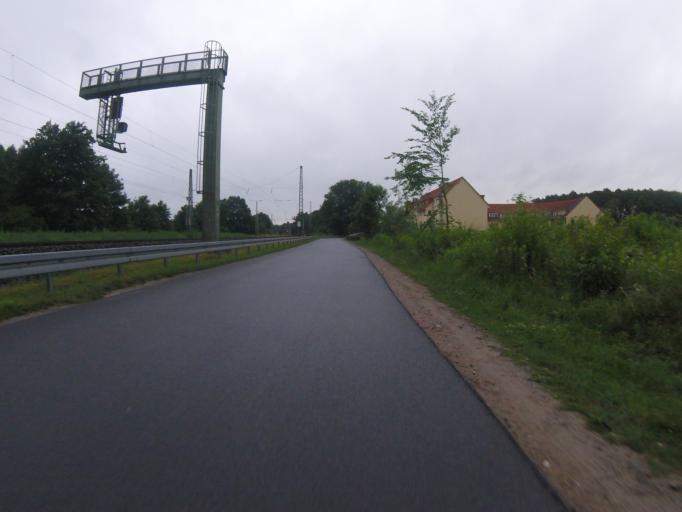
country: DE
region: Brandenburg
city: Bestensee
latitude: 52.2360
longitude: 13.6351
